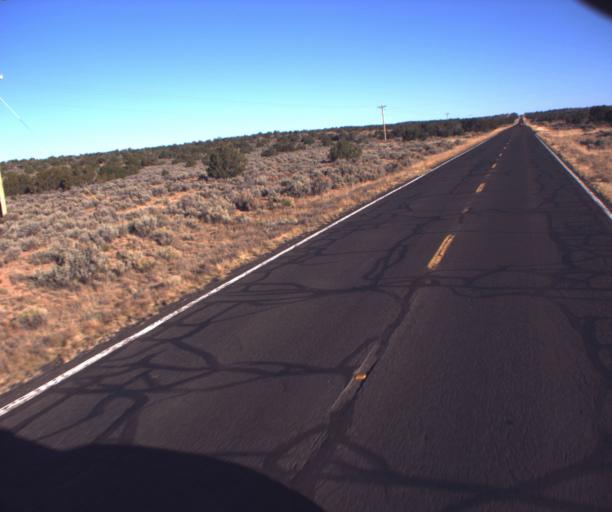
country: US
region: Arizona
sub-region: Apache County
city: Ganado
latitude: 35.5482
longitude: -109.5310
